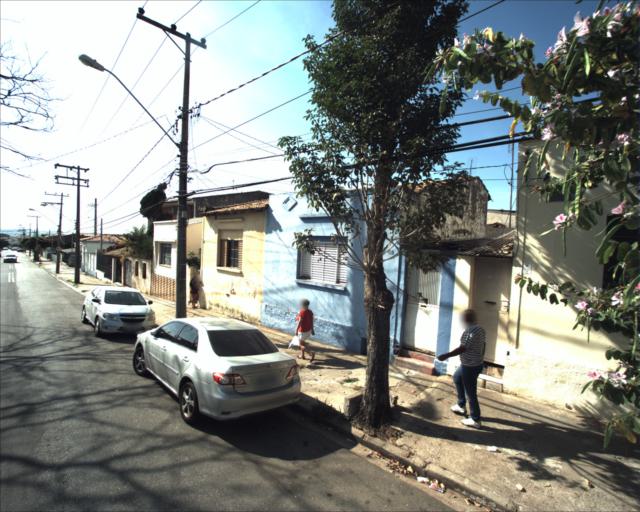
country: BR
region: Sao Paulo
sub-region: Sorocaba
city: Sorocaba
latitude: -23.4873
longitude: -47.4632
